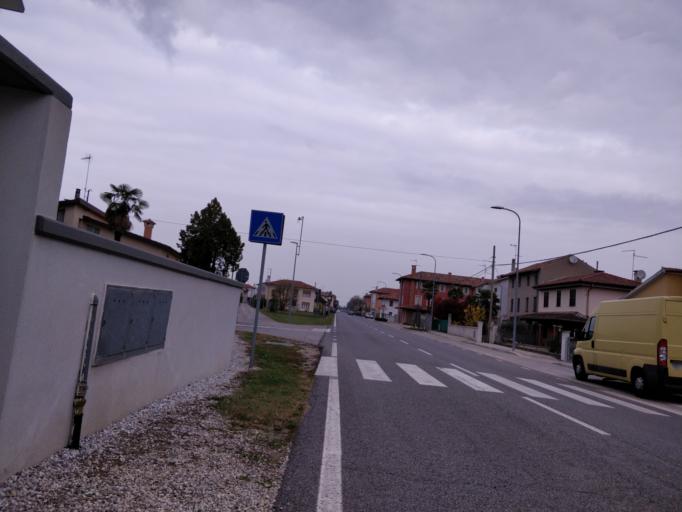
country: IT
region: Friuli Venezia Giulia
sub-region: Provincia di Udine
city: Bertiolo
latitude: 45.9457
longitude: 13.0554
